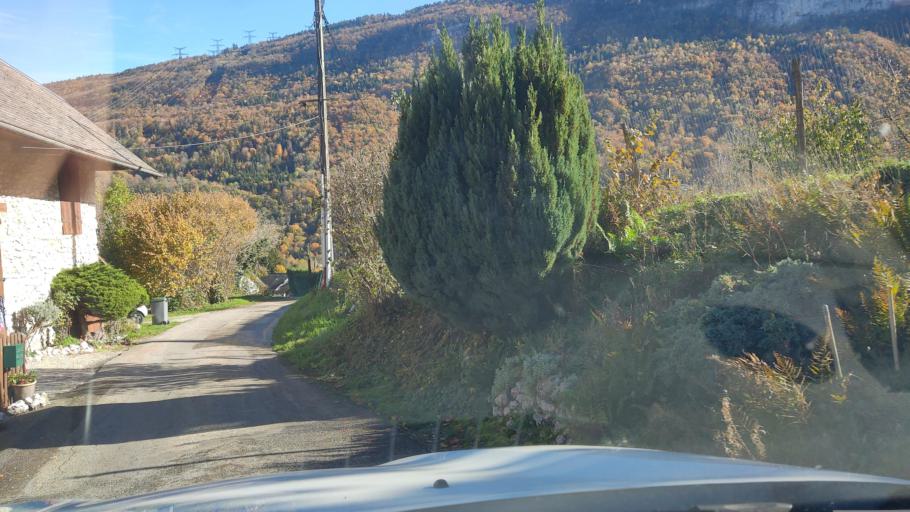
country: FR
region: Rhone-Alpes
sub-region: Departement de la Savoie
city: Vimines
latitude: 45.5130
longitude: 5.8418
